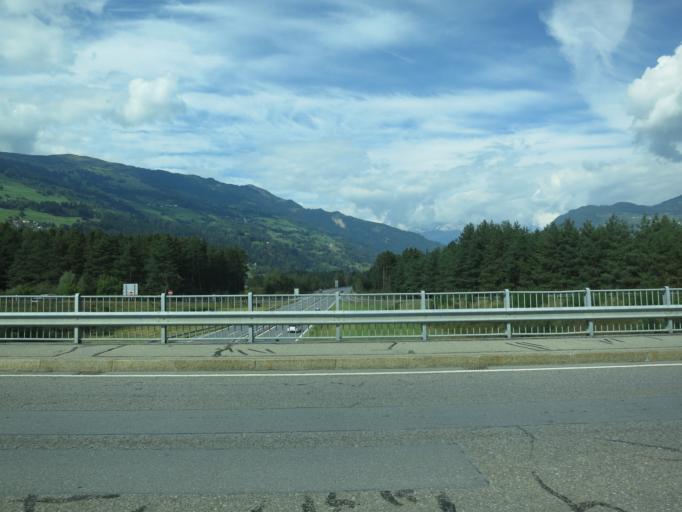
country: CH
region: Grisons
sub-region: Hinterrhein District
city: Thusis
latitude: 46.7144
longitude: 9.4455
